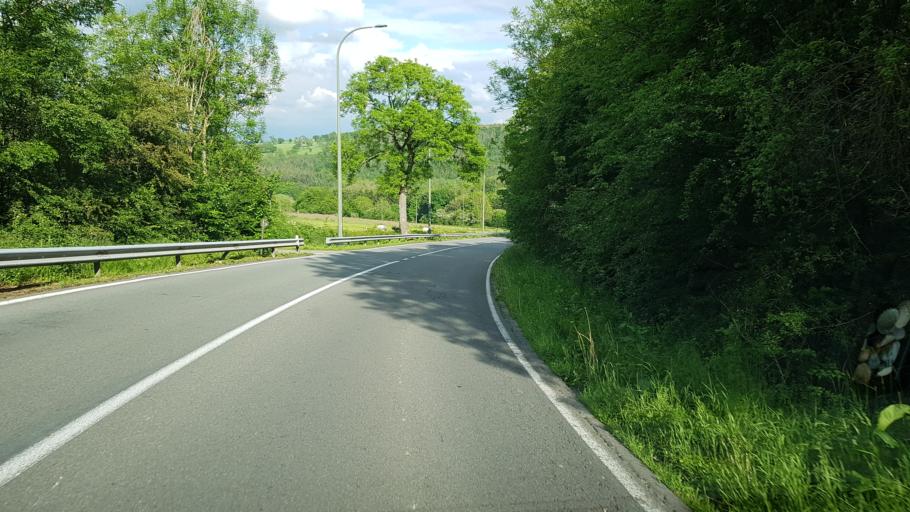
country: BE
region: Wallonia
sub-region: Province de Liege
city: Trooz
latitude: 50.5443
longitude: 5.6820
